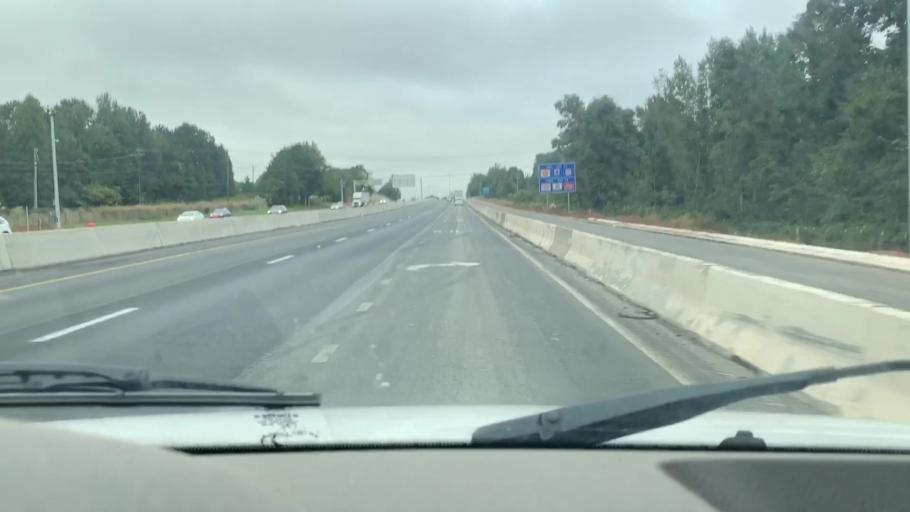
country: US
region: North Carolina
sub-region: Gaston County
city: Davidson
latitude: 35.5450
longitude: -80.8590
